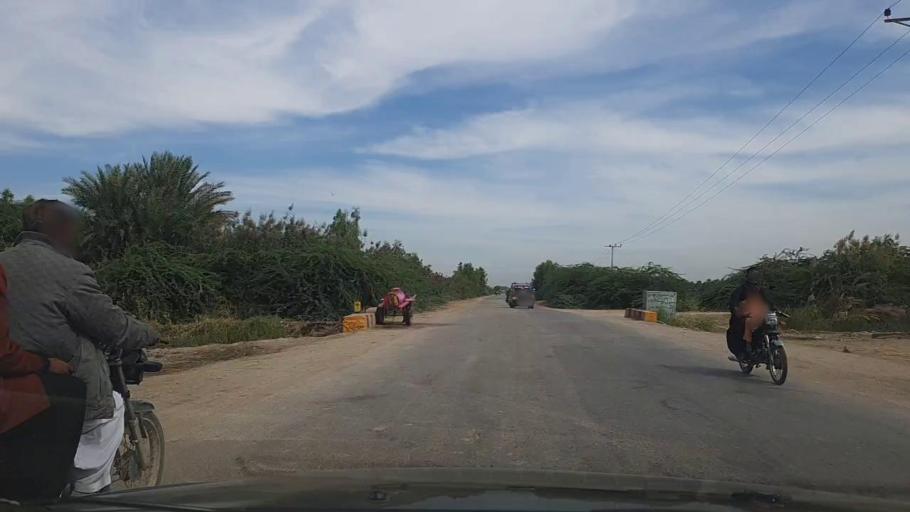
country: PK
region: Sindh
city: Thatta
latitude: 24.7584
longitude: 67.9308
